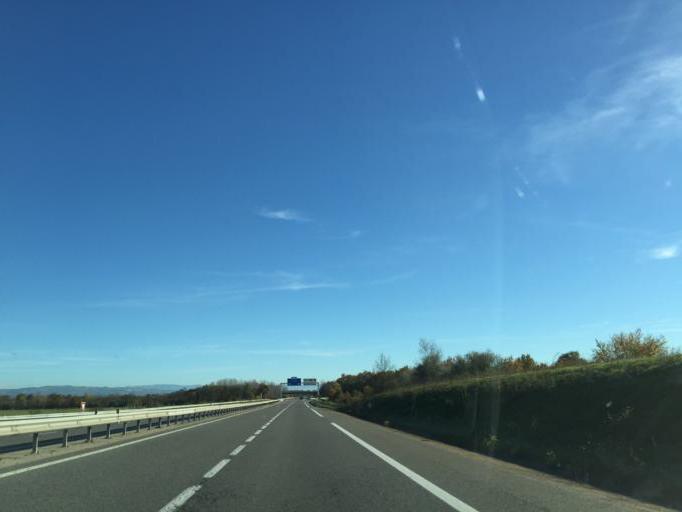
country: FR
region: Rhone-Alpes
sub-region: Departement de la Loire
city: Montrond-les-Bains
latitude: 45.6439
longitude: 4.1855
